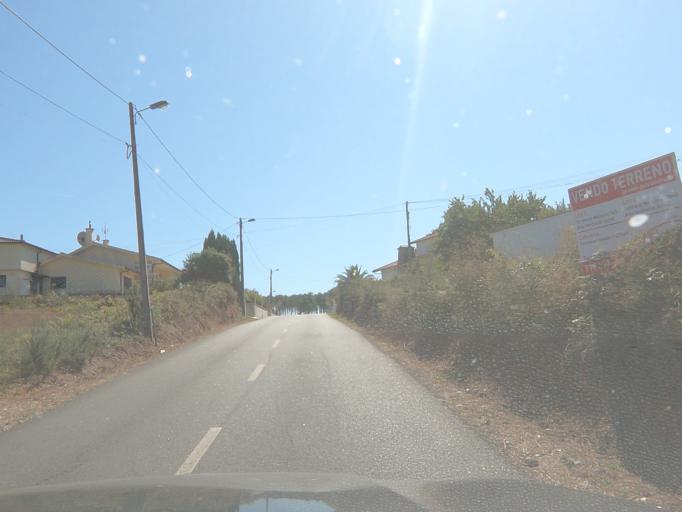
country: PT
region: Vila Real
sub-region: Vila Real
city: Vila Real
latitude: 41.2794
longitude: -7.7249
